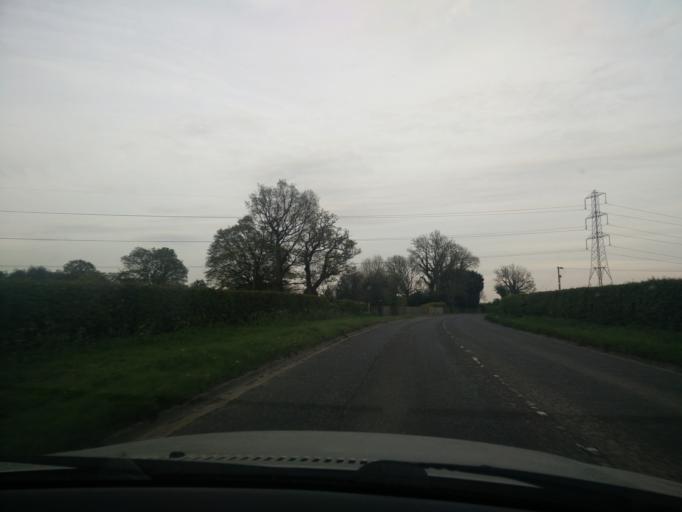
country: GB
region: England
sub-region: Buckinghamshire
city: Great Missenden
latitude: 51.7030
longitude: -0.6906
